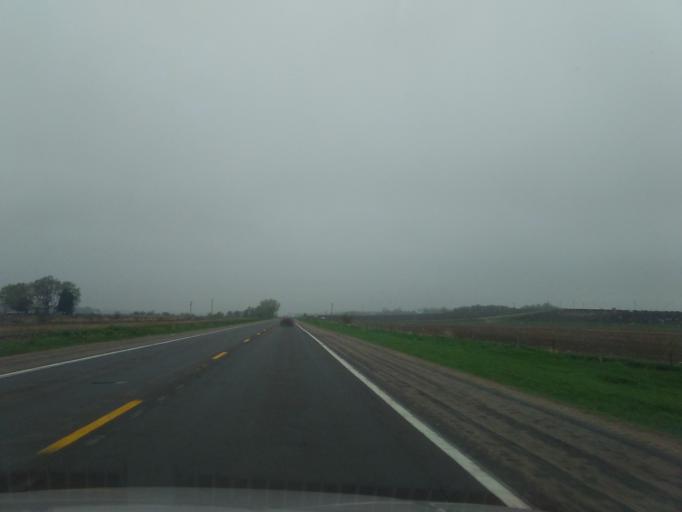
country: US
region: Nebraska
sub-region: Cuming County
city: Wisner
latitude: 41.9442
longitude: -96.8411
